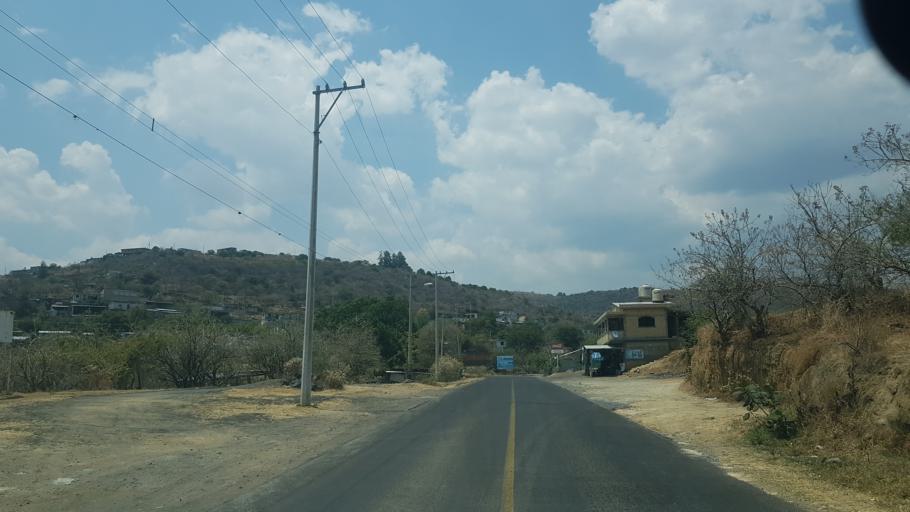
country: MX
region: Puebla
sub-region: Atzitzihuacan
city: Santiago Atzitzihuacan
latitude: 18.8351
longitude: -98.5946
